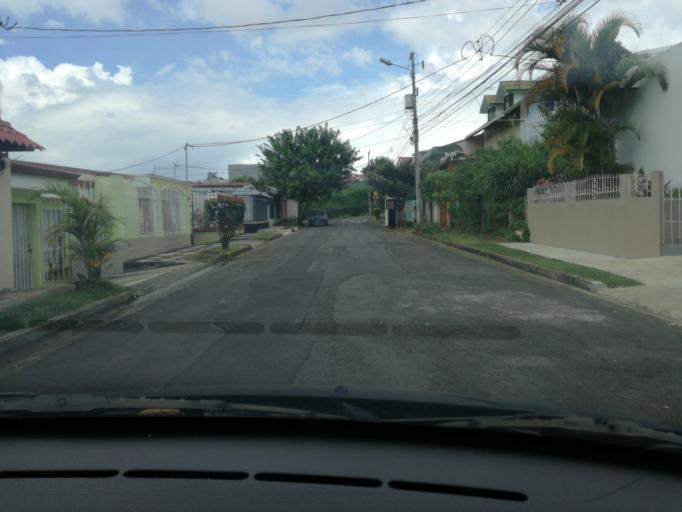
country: CR
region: San Jose
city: Curridabat
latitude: 9.9090
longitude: -84.0329
